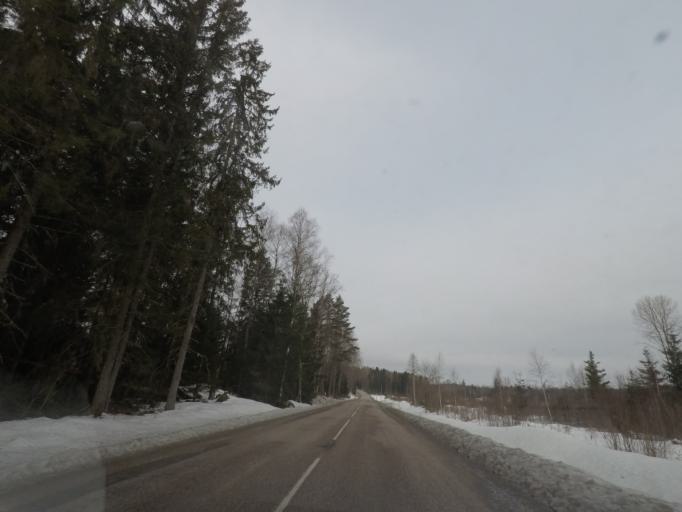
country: SE
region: Vaestmanland
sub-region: Vasteras
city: Skultuna
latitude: 59.7473
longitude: 16.3517
